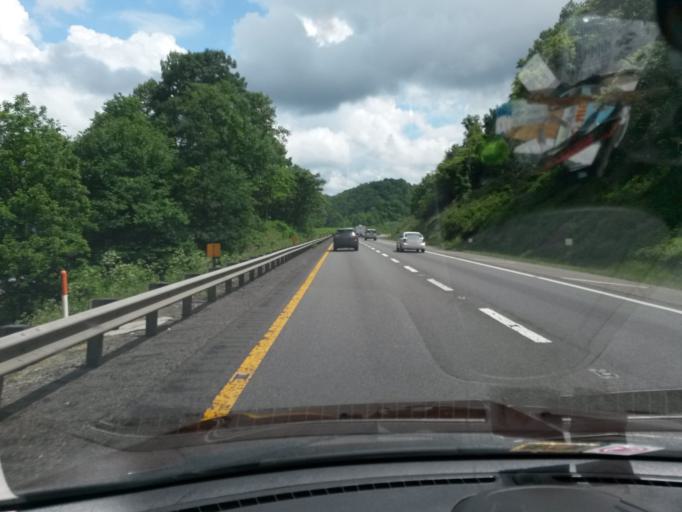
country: US
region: Virginia
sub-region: Carroll County
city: Cana
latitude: 36.6080
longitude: -80.7374
